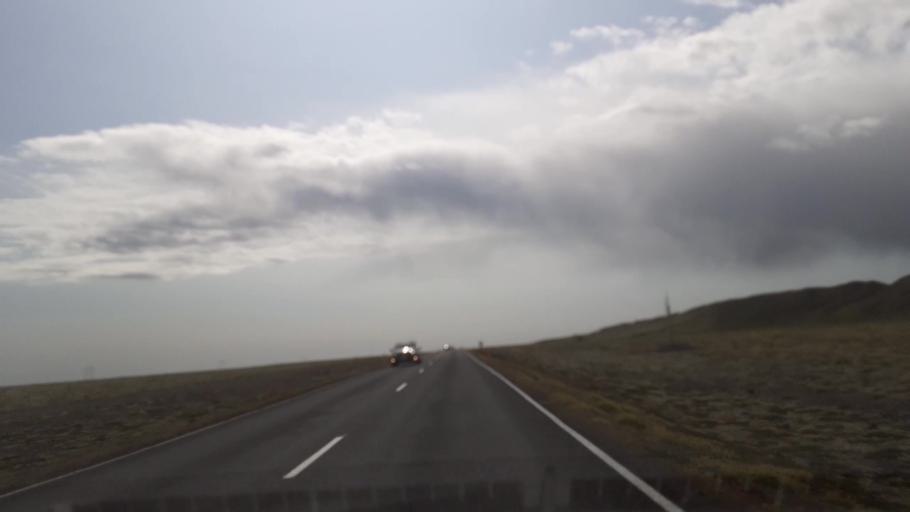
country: IS
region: East
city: Hoefn
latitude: 63.9602
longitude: -16.4239
